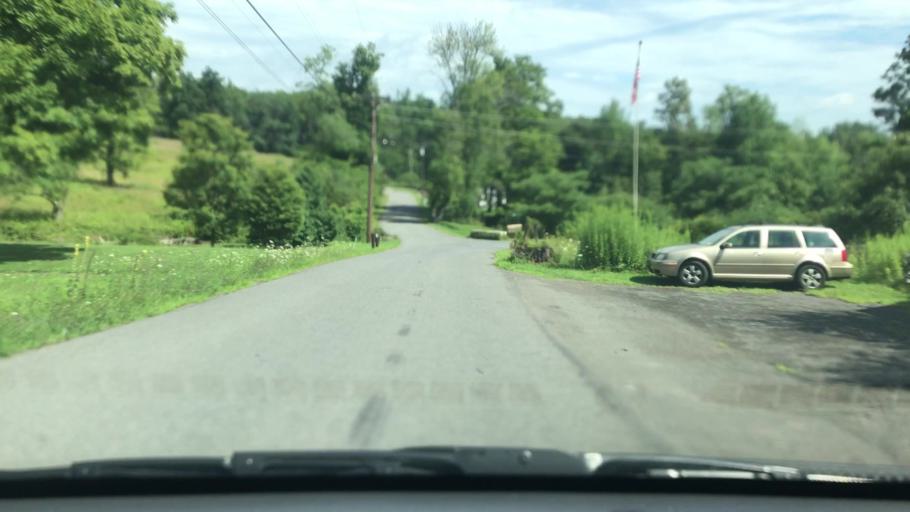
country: US
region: New York
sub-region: Ulster County
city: Shokan
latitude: 41.9533
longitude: -74.2761
